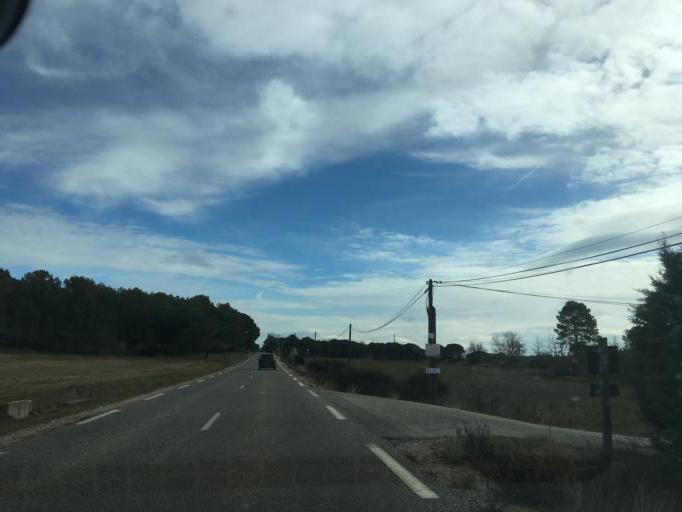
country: FR
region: Provence-Alpes-Cote d'Azur
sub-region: Departement du Var
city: La Celle
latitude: 43.4449
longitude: 6.0147
